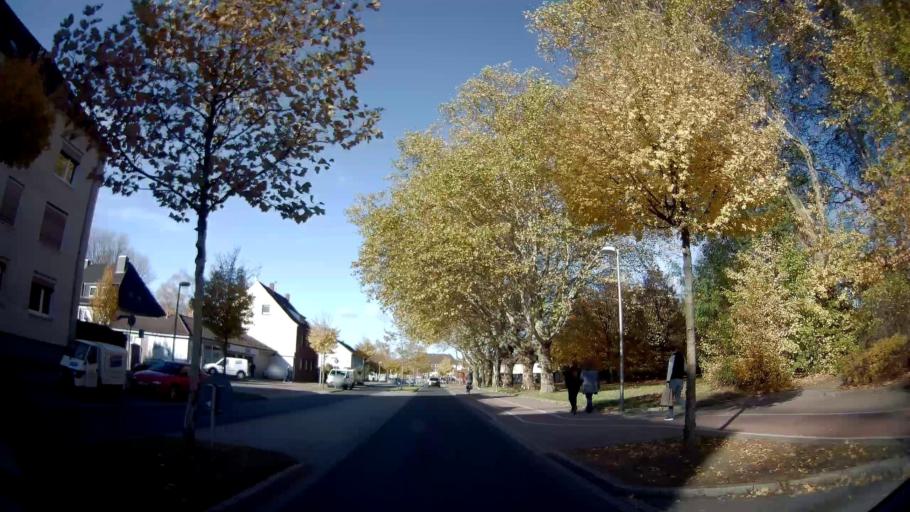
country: DE
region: North Rhine-Westphalia
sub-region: Regierungsbezirk Munster
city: Gladbeck
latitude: 51.5486
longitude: 7.0107
